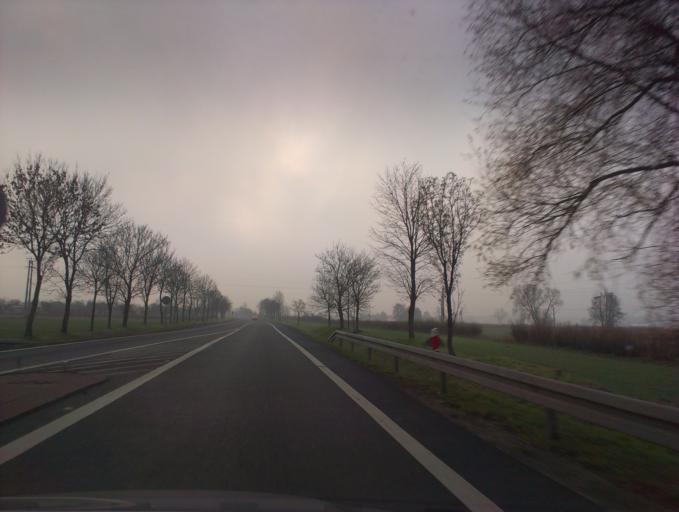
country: PL
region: Greater Poland Voivodeship
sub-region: Powiat chodzieski
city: Budzyn
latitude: 52.8892
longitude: 16.9697
